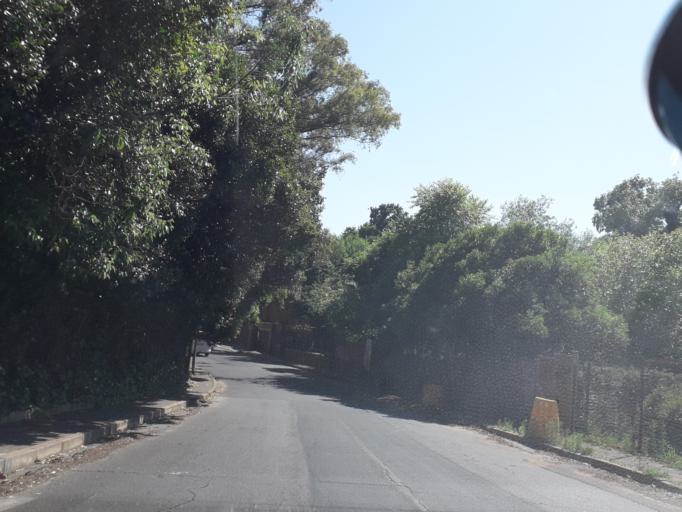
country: ZA
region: Gauteng
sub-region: City of Johannesburg Metropolitan Municipality
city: Johannesburg
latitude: -26.1451
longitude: 28.0161
